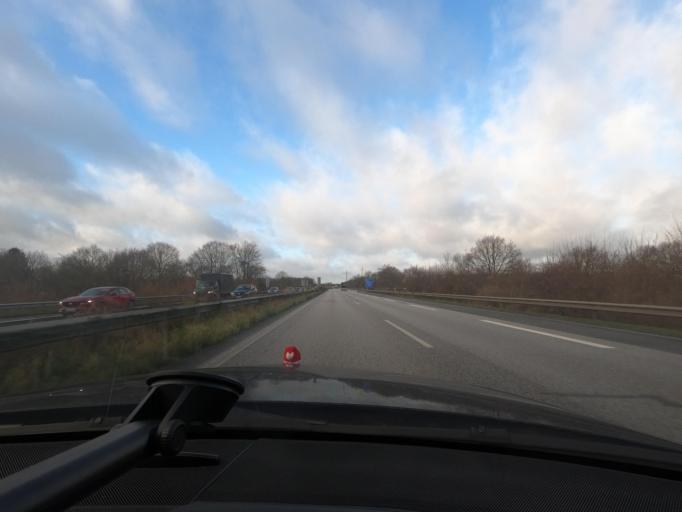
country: DE
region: Schleswig-Holstein
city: Borgstedt
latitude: 54.3429
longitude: 9.7076
